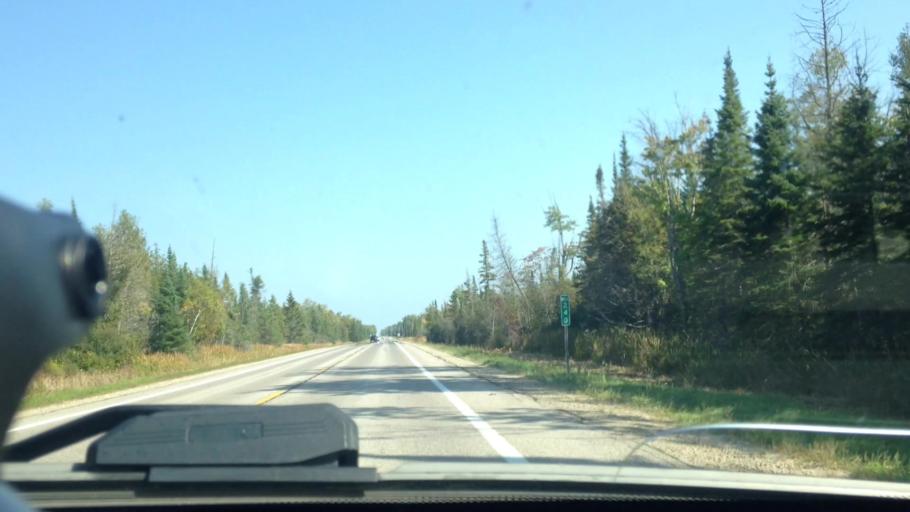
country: US
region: Michigan
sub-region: Luce County
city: Newberry
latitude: 46.3035
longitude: -85.3877
